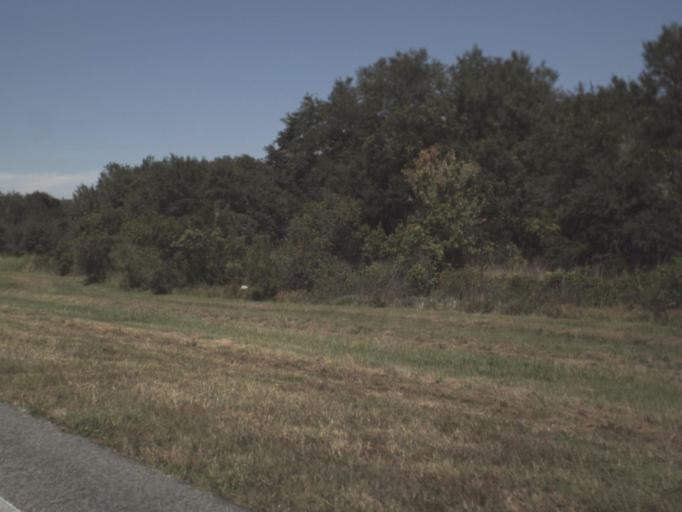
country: US
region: Florida
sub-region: Highlands County
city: Placid Lakes
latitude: 27.0061
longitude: -81.3320
